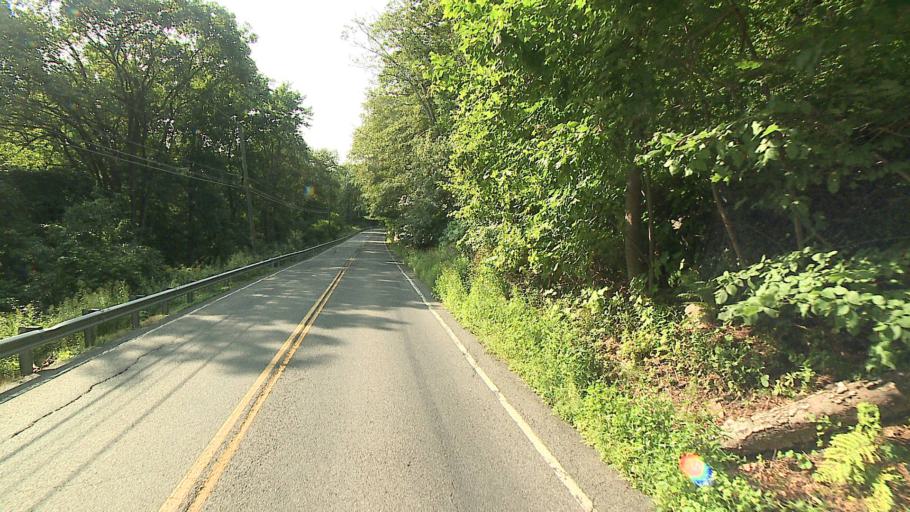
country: US
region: Connecticut
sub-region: Litchfield County
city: Canaan
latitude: 41.8769
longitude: -73.3674
